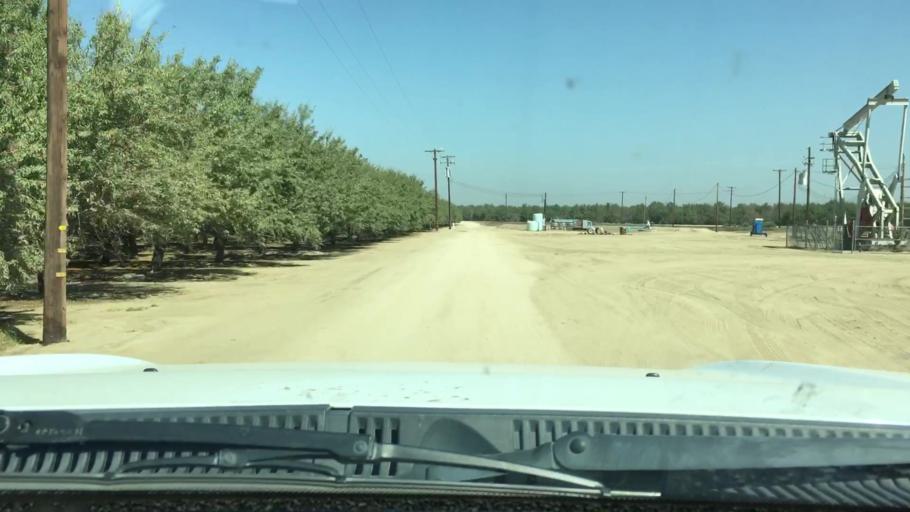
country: US
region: California
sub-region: Kern County
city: Shafter
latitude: 35.5373
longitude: -119.2689
